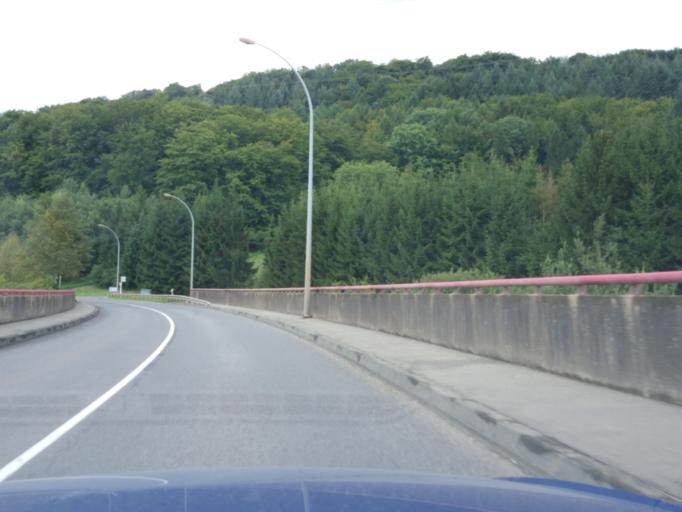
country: LU
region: Luxembourg
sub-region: Canton de Mersch
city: Mersch
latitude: 49.7360
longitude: 6.0968
